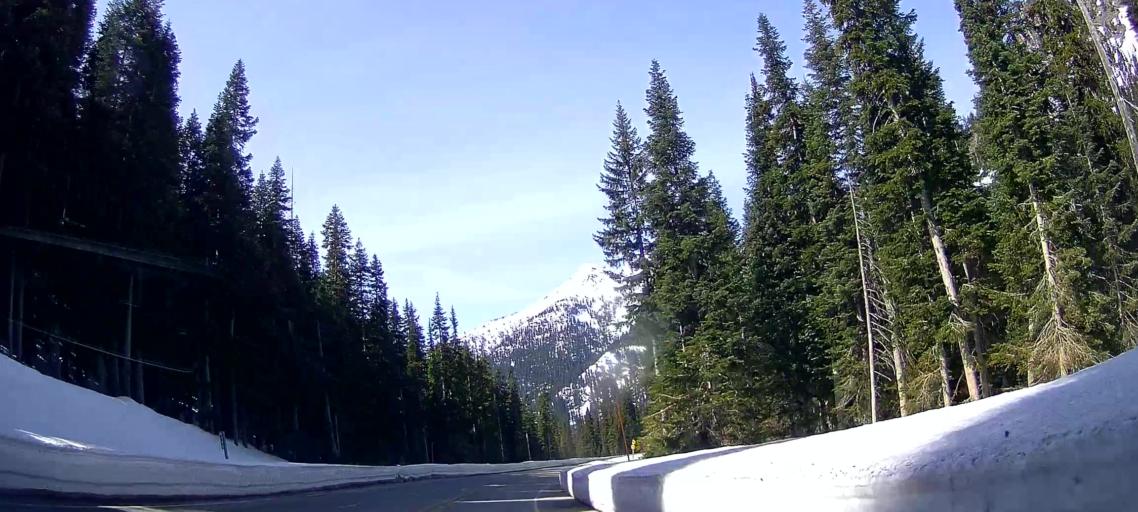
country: US
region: Washington
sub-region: Chelan County
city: Granite Falls
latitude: 48.5058
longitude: -120.6990
